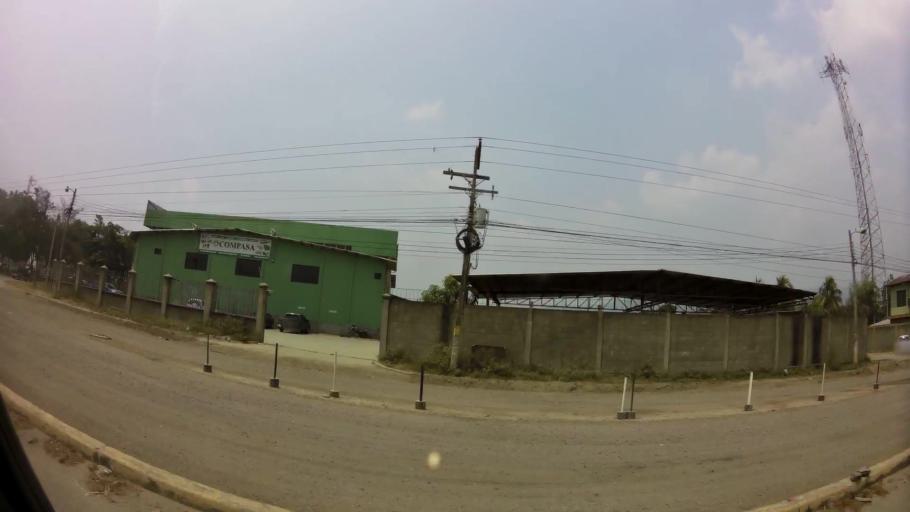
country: HN
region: Cortes
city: San Pedro Sula
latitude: 15.4790
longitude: -88.0081
